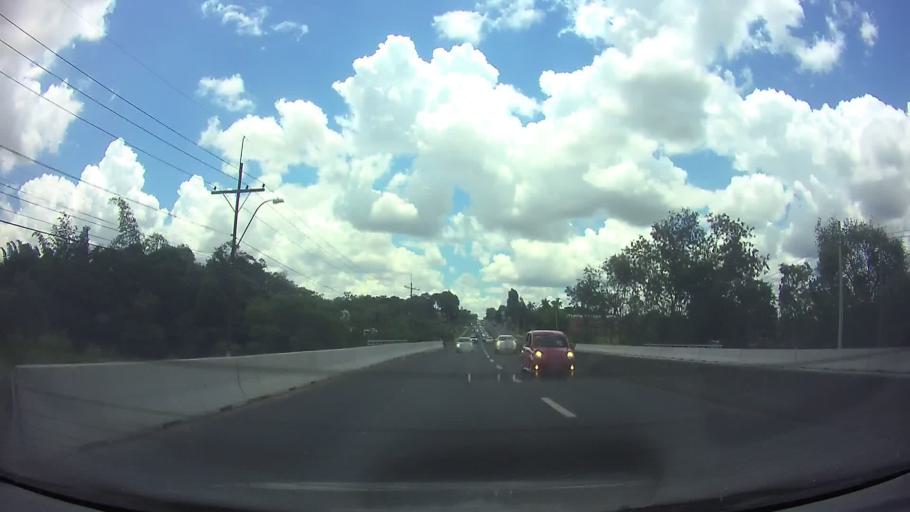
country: PY
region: Central
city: Capiata
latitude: -25.3771
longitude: -57.4040
